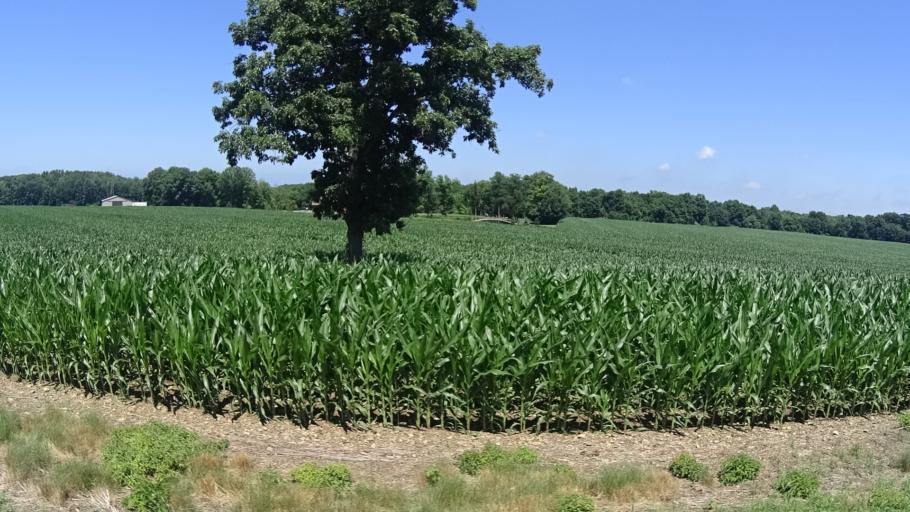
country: US
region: Ohio
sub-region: Lorain County
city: Vermilion
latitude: 41.3525
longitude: -82.4305
